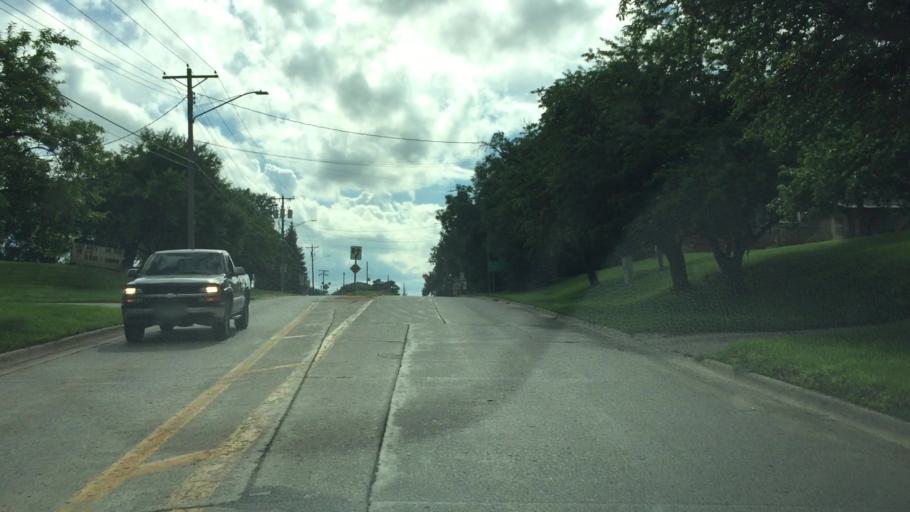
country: US
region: Iowa
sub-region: Jasper County
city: Newton
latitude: 41.6992
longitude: -93.0733
